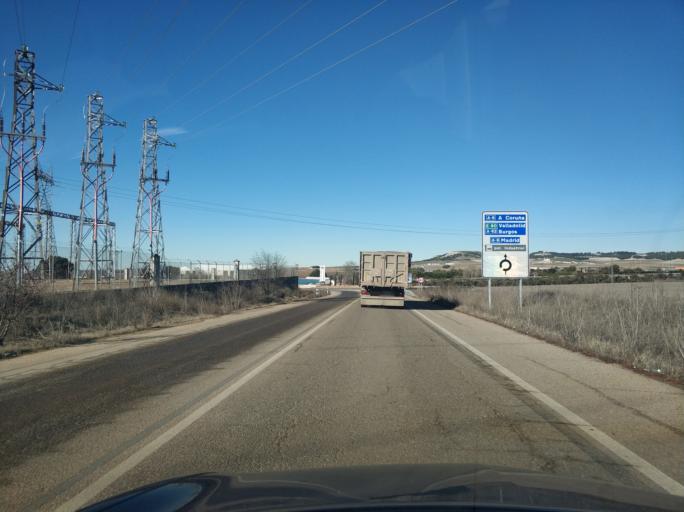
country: ES
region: Castille and Leon
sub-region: Provincia de Valladolid
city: Tordesillas
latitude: 41.5079
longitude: -5.0124
